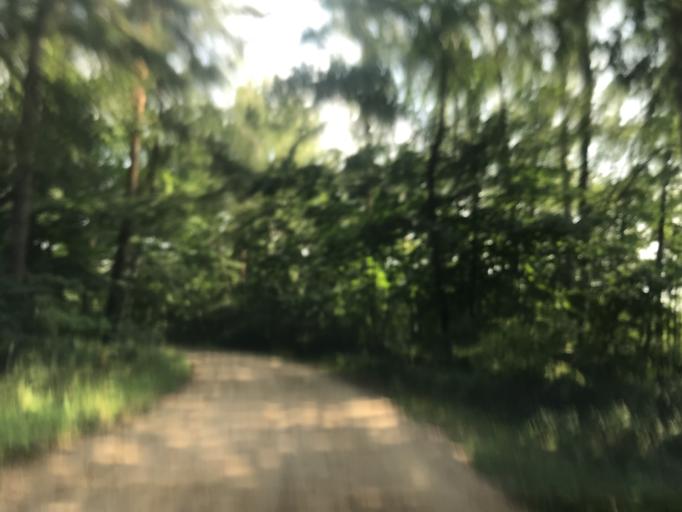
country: PL
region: Kujawsko-Pomorskie
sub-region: Powiat brodnicki
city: Brodnica
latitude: 53.3591
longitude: 19.4547
